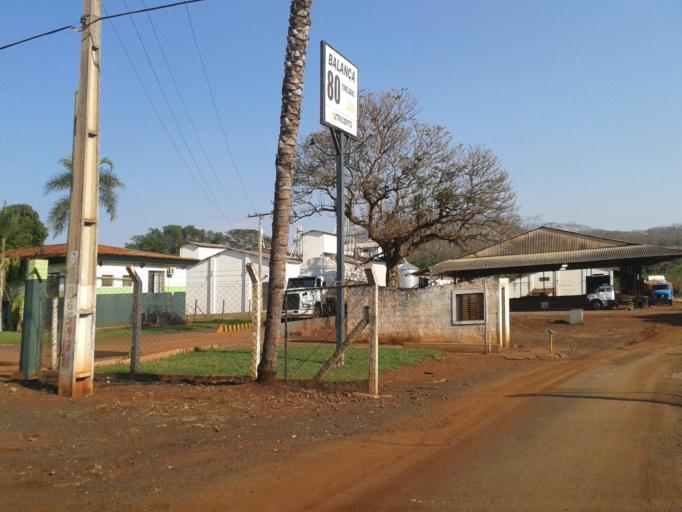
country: BR
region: Minas Gerais
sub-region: Ituiutaba
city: Ituiutaba
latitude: -18.9467
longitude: -49.4583
